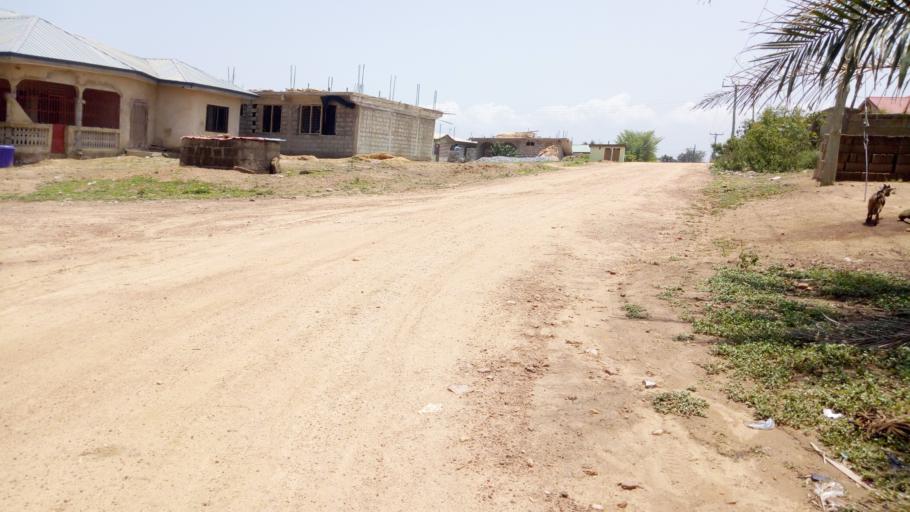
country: GH
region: Central
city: Kasoa
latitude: 5.5027
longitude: -0.4490
